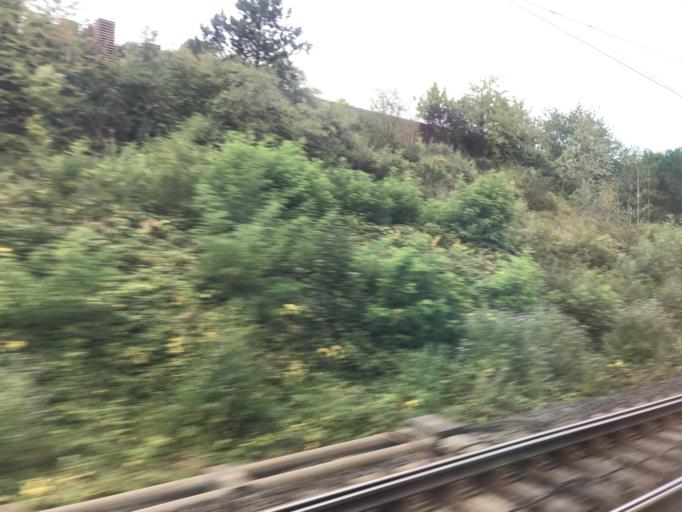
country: DE
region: North Rhine-Westphalia
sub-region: Regierungsbezirk Koln
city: Kerpen
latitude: 50.9208
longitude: 6.7256
